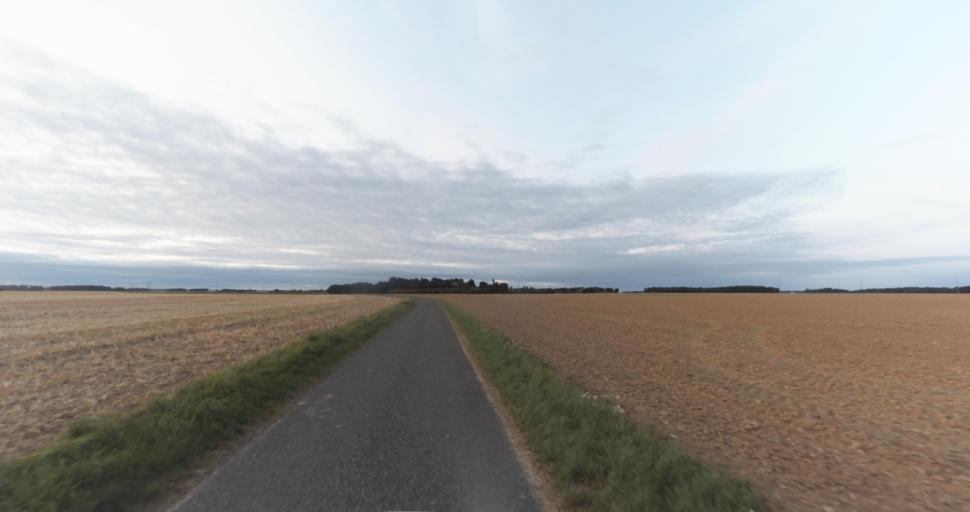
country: FR
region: Haute-Normandie
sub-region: Departement de l'Eure
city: La Madeleine-de-Nonancourt
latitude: 48.8727
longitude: 1.2311
